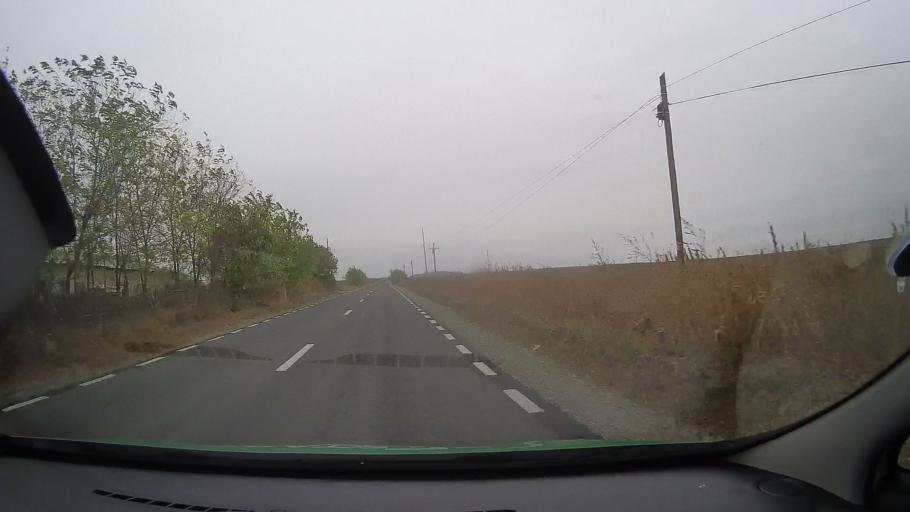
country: RO
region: Constanta
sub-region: Comuna Tortoman
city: Tortoman
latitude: 44.3637
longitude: 28.2092
